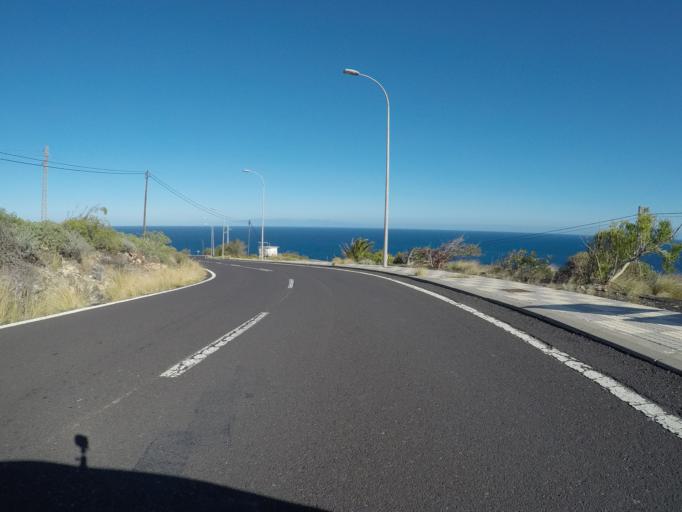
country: ES
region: Canary Islands
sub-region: Provincia de Santa Cruz de Tenerife
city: Fasnia
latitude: 28.2225
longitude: -16.4178
